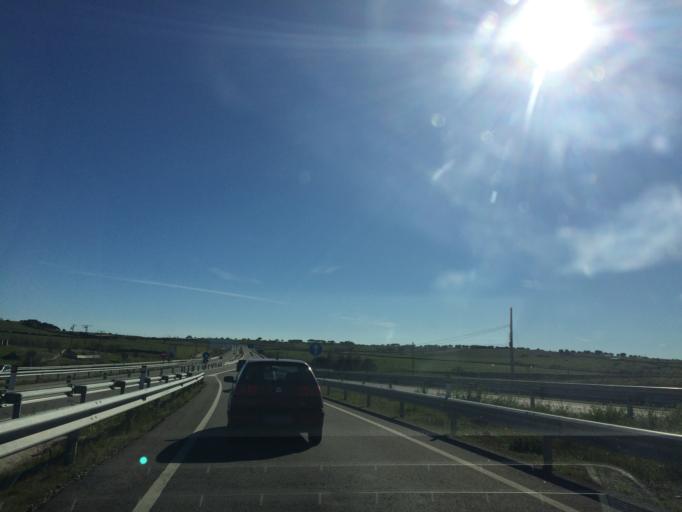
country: ES
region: Madrid
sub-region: Provincia de Madrid
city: Colmenar Viejo
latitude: 40.7131
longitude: -3.7939
